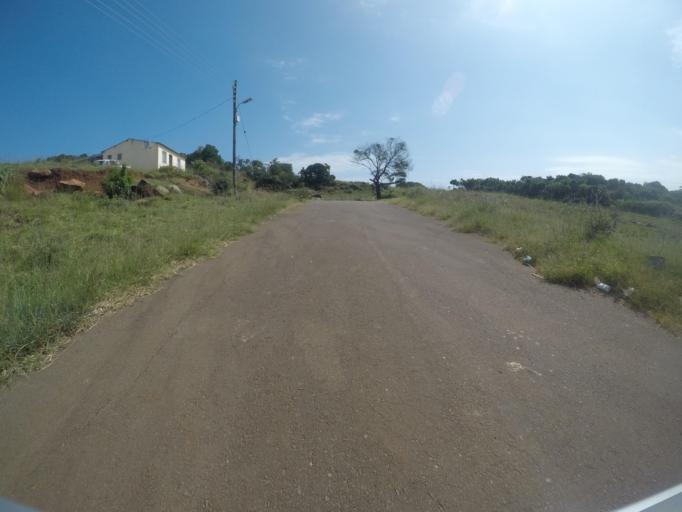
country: ZA
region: Eastern Cape
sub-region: Buffalo City Metropolitan Municipality
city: East London
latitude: -32.9638
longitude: 27.8776
